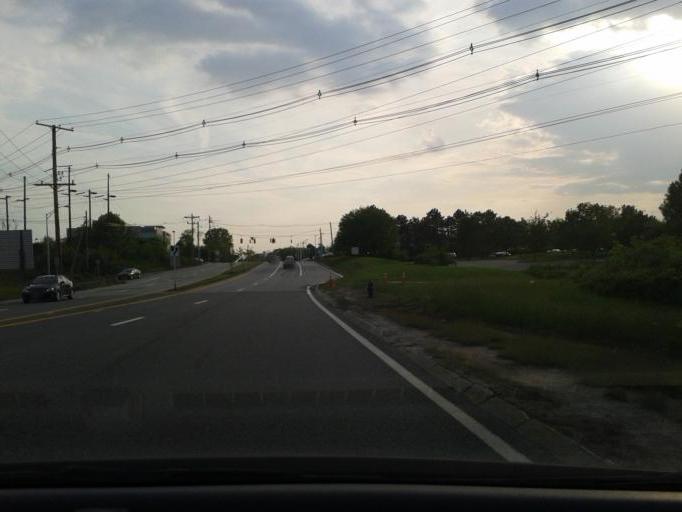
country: US
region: Massachusetts
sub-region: Middlesex County
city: Cochituate
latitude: 42.3071
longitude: -71.3896
